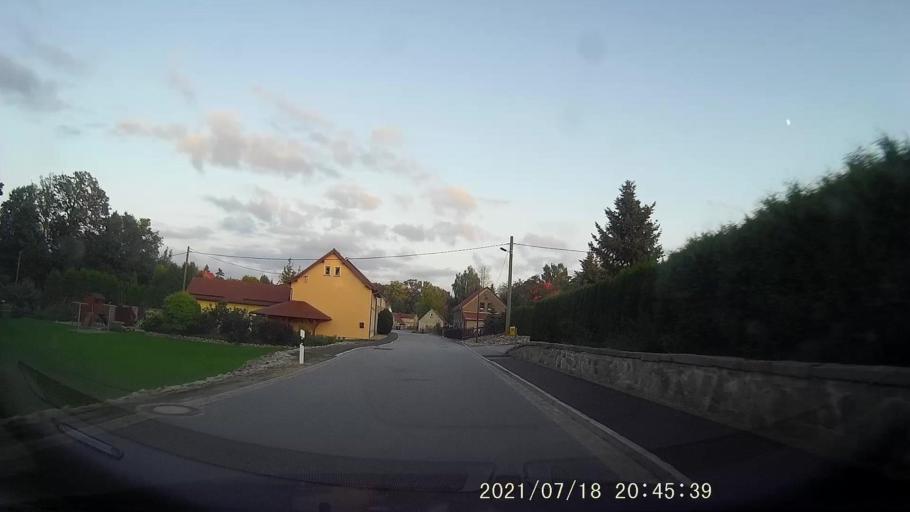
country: DE
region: Saxony
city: Reichenbach
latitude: 51.1946
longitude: 14.7867
